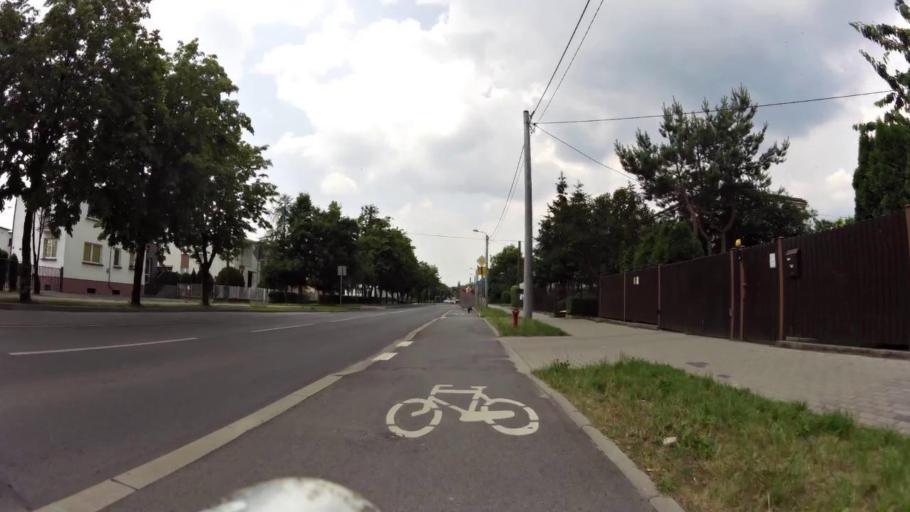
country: PL
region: Kujawsko-Pomorskie
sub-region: Powiat bydgoski
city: Koronowo
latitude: 53.3067
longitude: 17.9446
